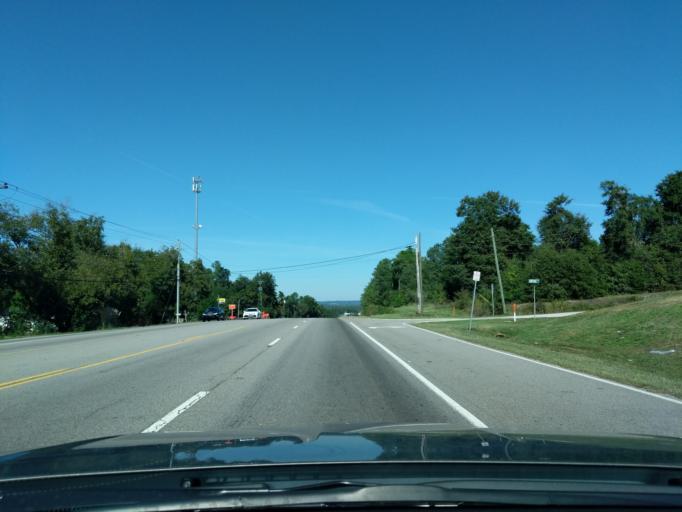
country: US
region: Georgia
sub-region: Richmond County
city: Augusta
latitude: 33.3755
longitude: -82.0000
